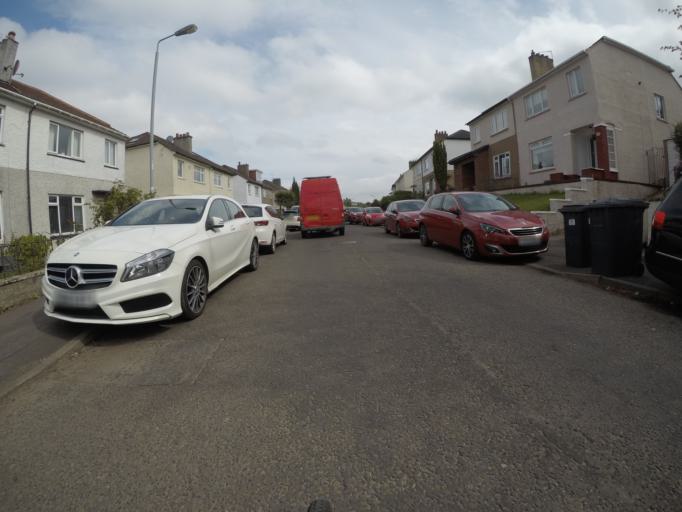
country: GB
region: Scotland
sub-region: East Renfrewshire
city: Giffnock
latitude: 55.8070
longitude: -4.2807
